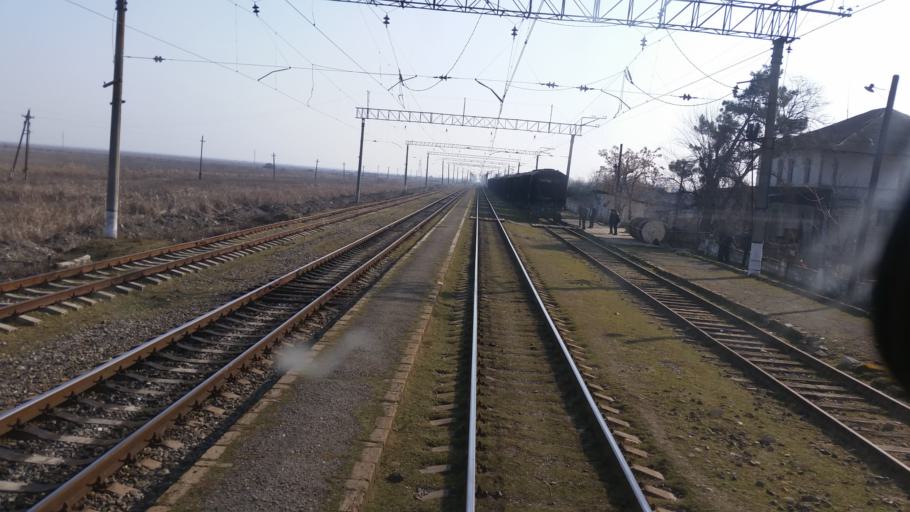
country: AZ
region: Kurdamir Rayon
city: Kyurdarmir
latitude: 40.3916
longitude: 48.0392
